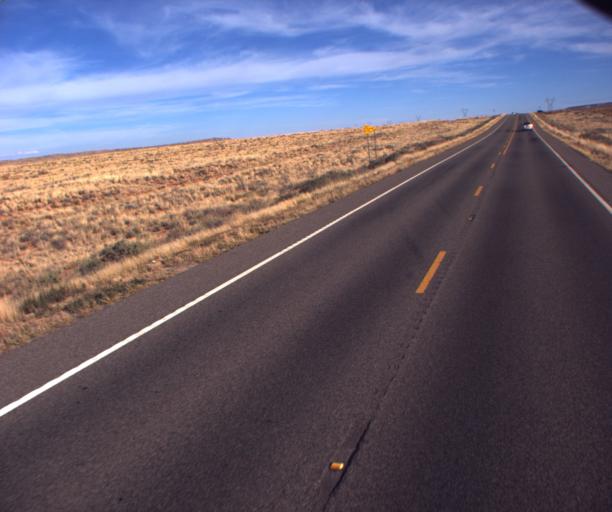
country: US
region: Arizona
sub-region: Apache County
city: Lukachukai
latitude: 36.9402
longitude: -109.2501
